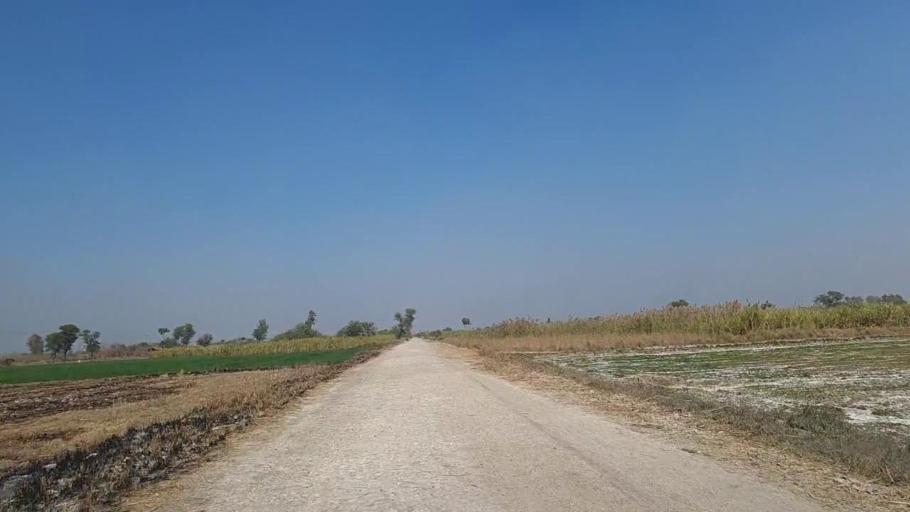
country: PK
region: Sindh
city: Daur
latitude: 26.4901
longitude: 68.3385
